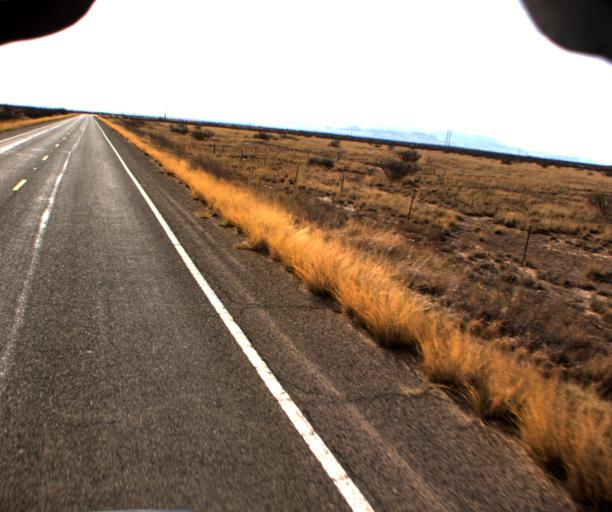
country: US
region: Arizona
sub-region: Cochise County
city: Willcox
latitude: 32.1953
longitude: -109.7499
